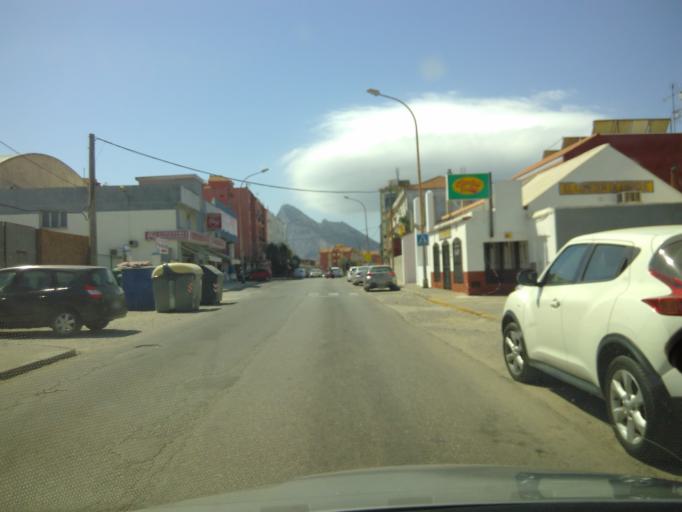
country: ES
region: Andalusia
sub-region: Provincia de Cadiz
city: La Linea de la Concepcion
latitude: 36.1740
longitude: -5.3485
